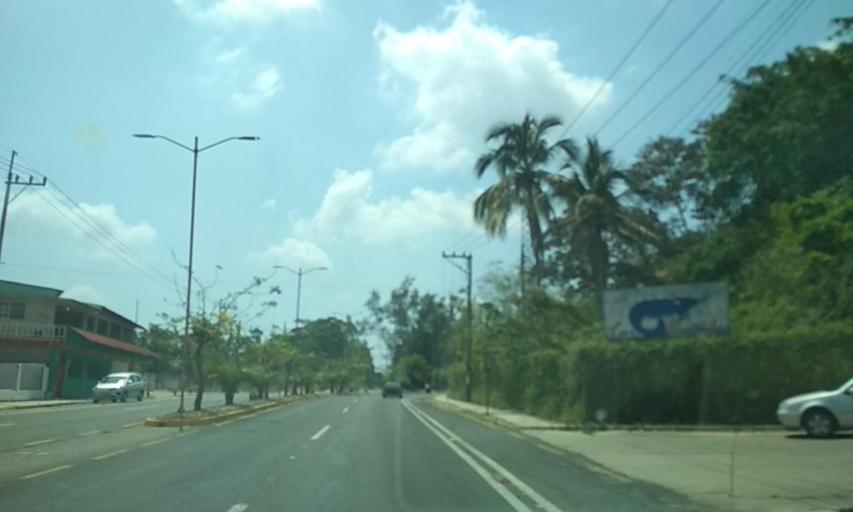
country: MX
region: Veracruz
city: Las Choapas
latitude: 17.9323
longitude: -94.0989
